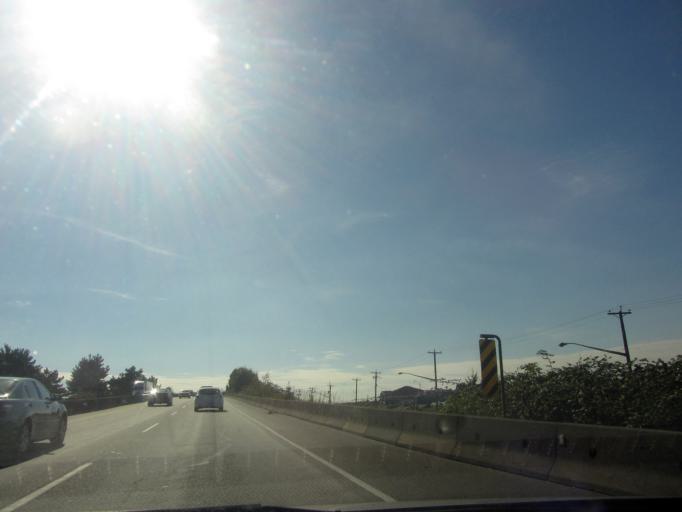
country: CA
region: British Columbia
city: Delta
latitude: 49.1697
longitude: -122.9946
